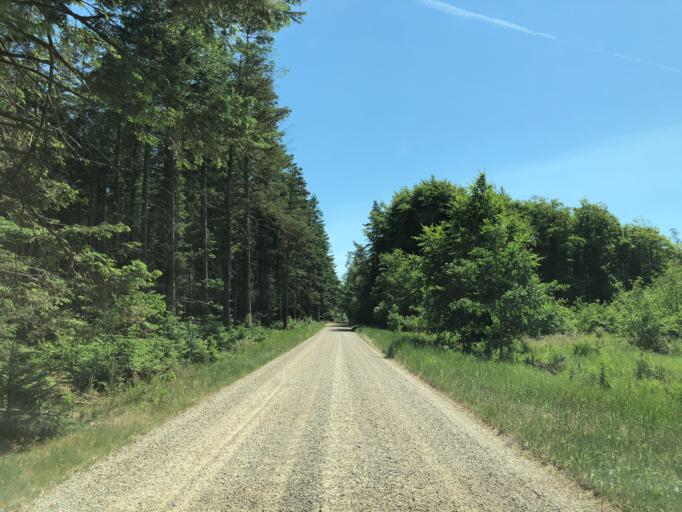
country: DK
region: Central Jutland
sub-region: Struer Kommune
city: Struer
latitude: 56.4366
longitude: 8.4443
